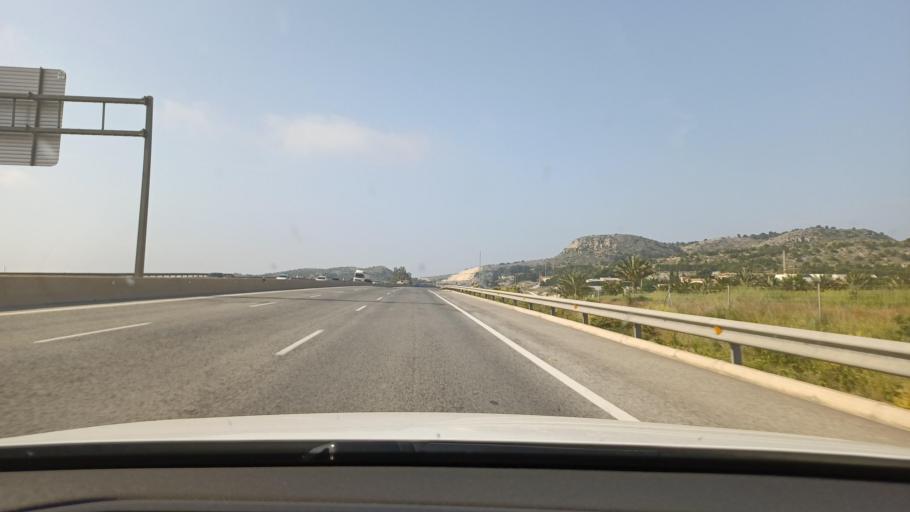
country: ES
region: Valencia
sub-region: Provincia de Alicante
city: Elche
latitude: 38.3274
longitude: -0.6630
